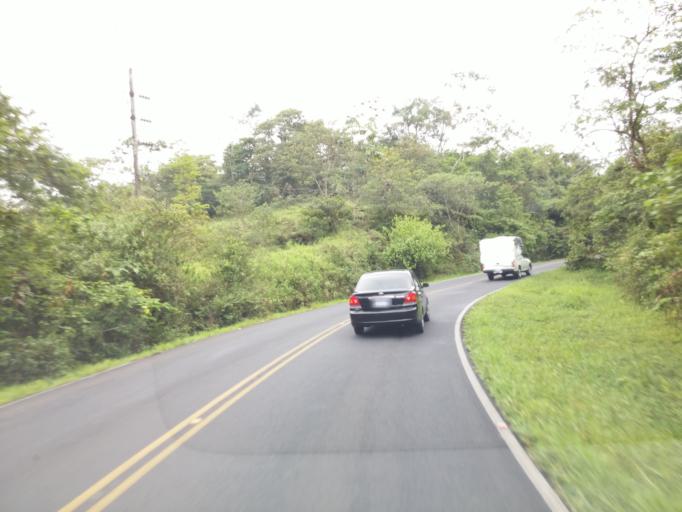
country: CR
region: Alajuela
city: Quesada
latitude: 10.2242
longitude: -84.5375
